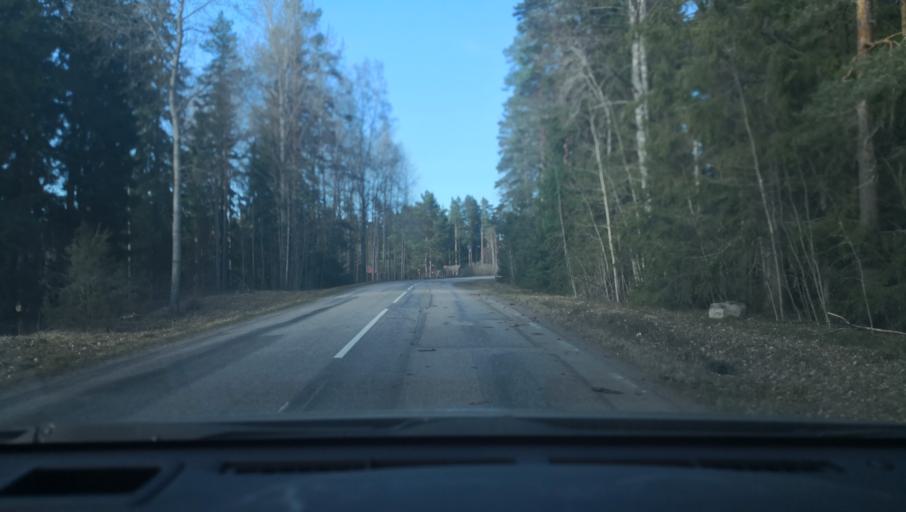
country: SE
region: Uppsala
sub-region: Heby Kommun
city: Heby
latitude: 59.9810
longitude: 16.9073
